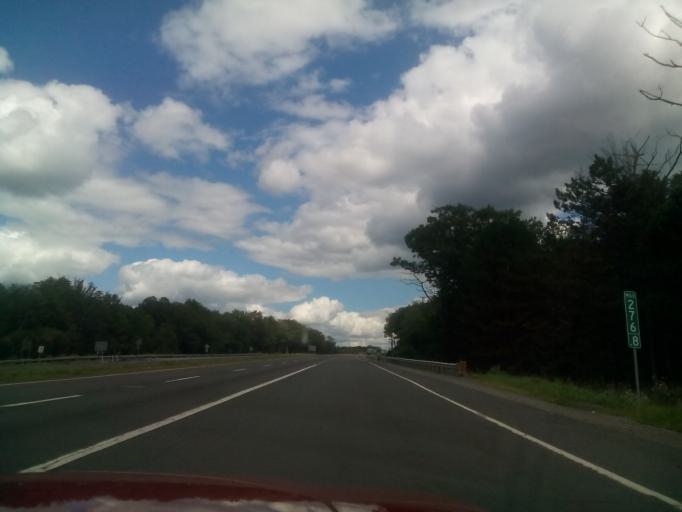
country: US
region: Pennsylvania
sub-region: Luzerne County
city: White Haven
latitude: 41.0664
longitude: -75.7014
